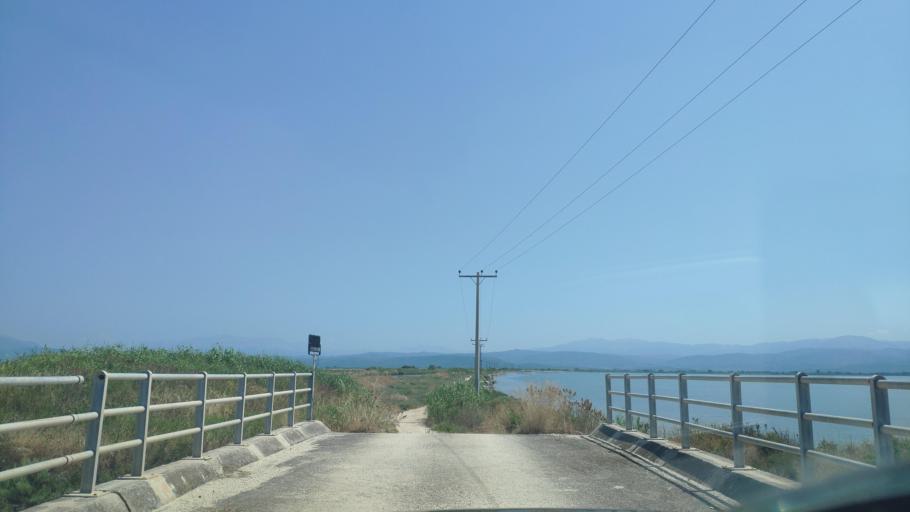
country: GR
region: Epirus
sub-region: Nomos Artas
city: Aneza
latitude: 39.0204
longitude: 20.9332
